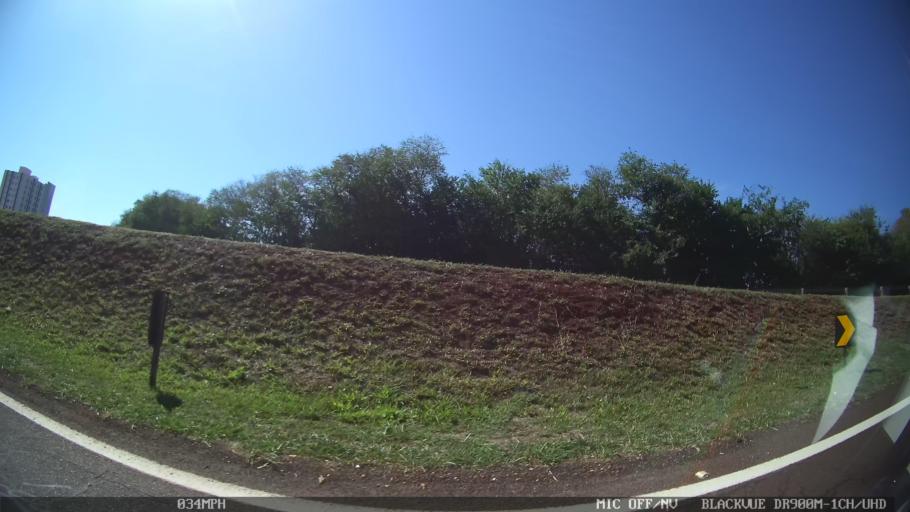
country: BR
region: Sao Paulo
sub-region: Ribeirao Preto
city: Ribeirao Preto
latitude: -21.2222
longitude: -47.8158
